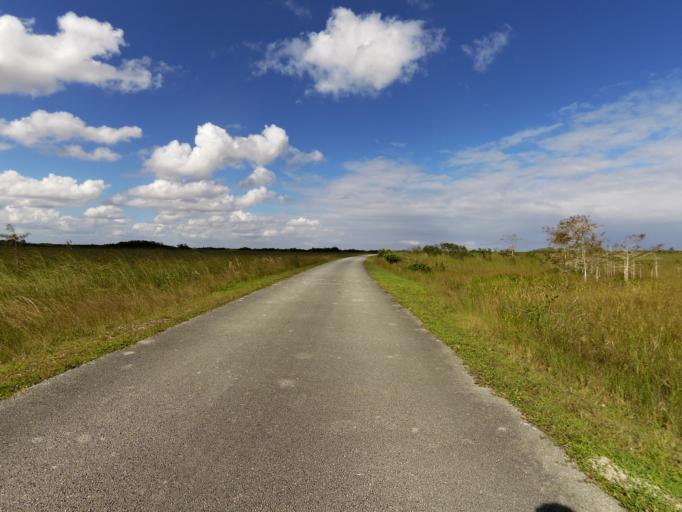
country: US
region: Florida
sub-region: Miami-Dade County
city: The Hammocks
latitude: 25.7350
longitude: -80.7598
